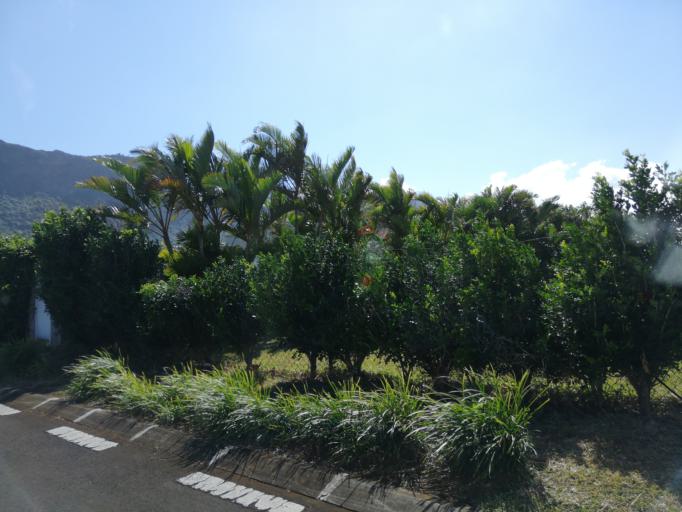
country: MU
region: Moka
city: Moka
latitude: -20.2222
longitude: 57.4978
